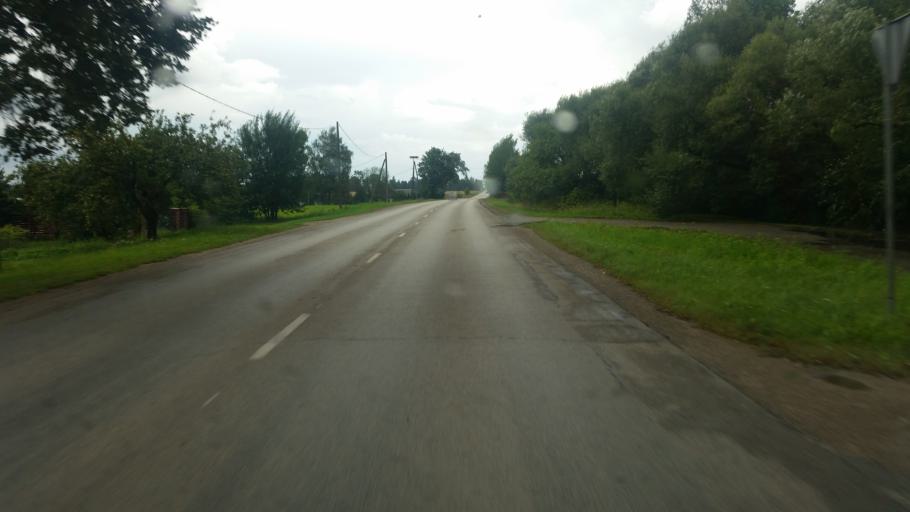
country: LV
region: Bauskas Rajons
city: Bauska
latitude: 56.4210
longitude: 24.2138
